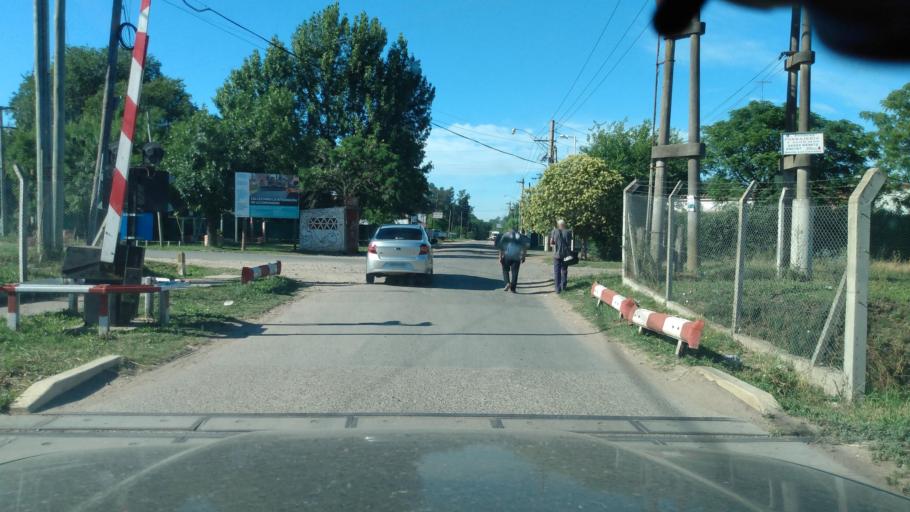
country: AR
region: Buenos Aires
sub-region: Partido de Lujan
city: Lujan
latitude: -34.5845
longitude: -59.0575
